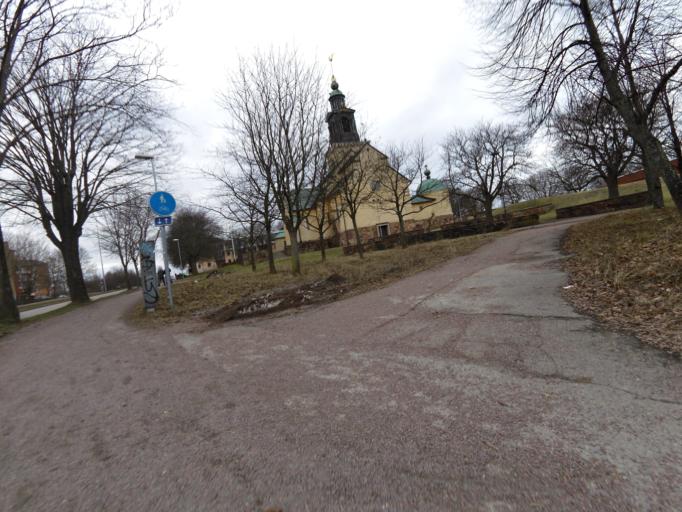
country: SE
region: Gaevleborg
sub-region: Gavle Kommun
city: Gavle
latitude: 60.6708
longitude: 17.1644
